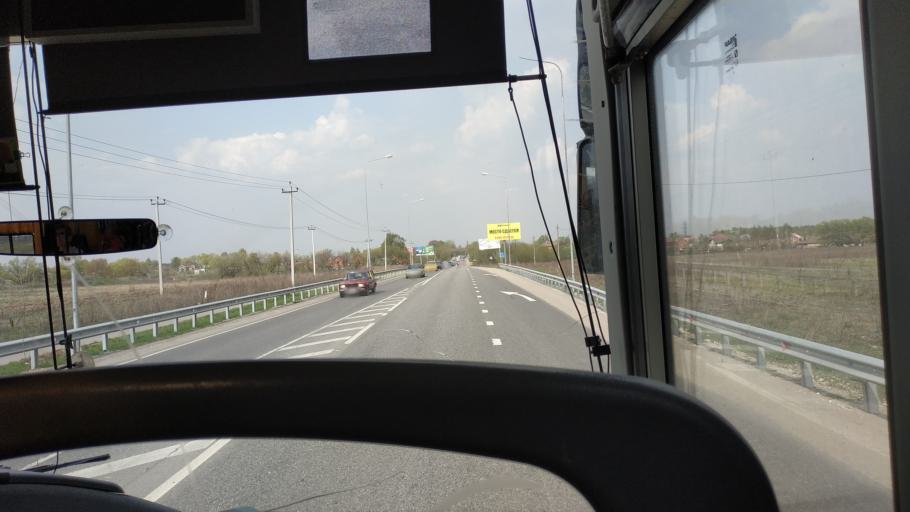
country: RU
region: Moskovskaya
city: Tomilino
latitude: 55.6228
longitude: 37.9244
